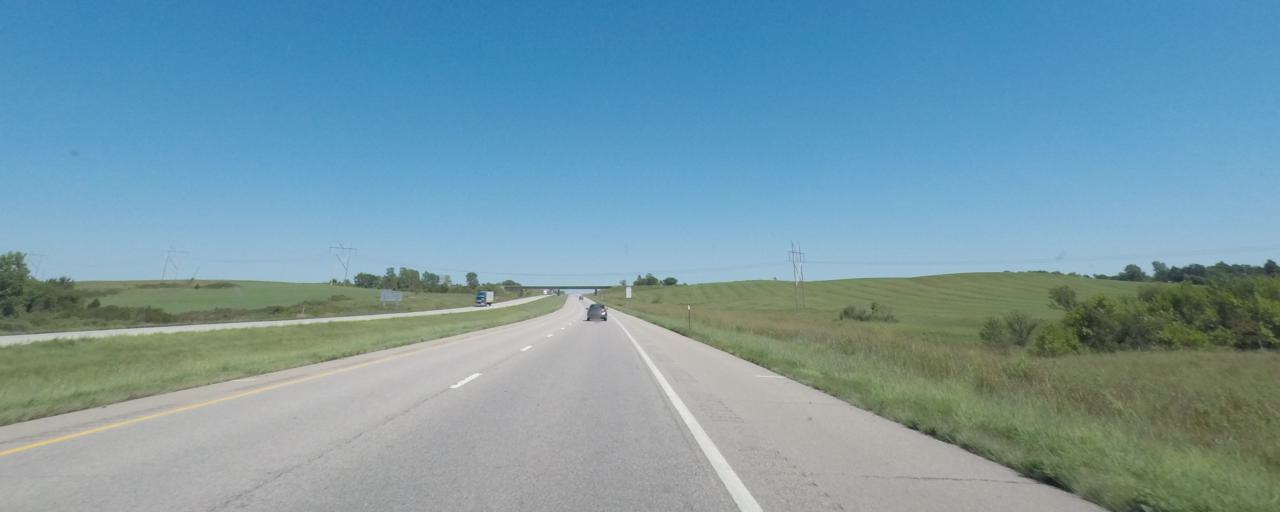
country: US
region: Kansas
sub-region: Lyon County
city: Emporia
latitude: 38.4102
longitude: -96.0856
